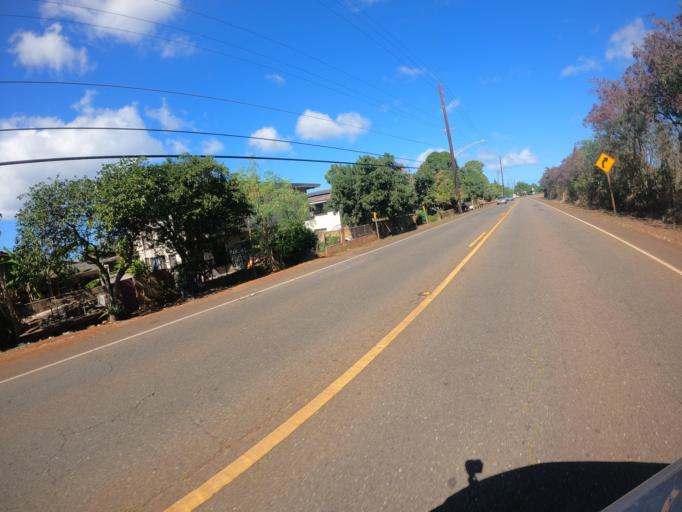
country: US
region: Hawaii
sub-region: Honolulu County
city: Hale'iwa
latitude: 21.5739
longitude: -158.1075
